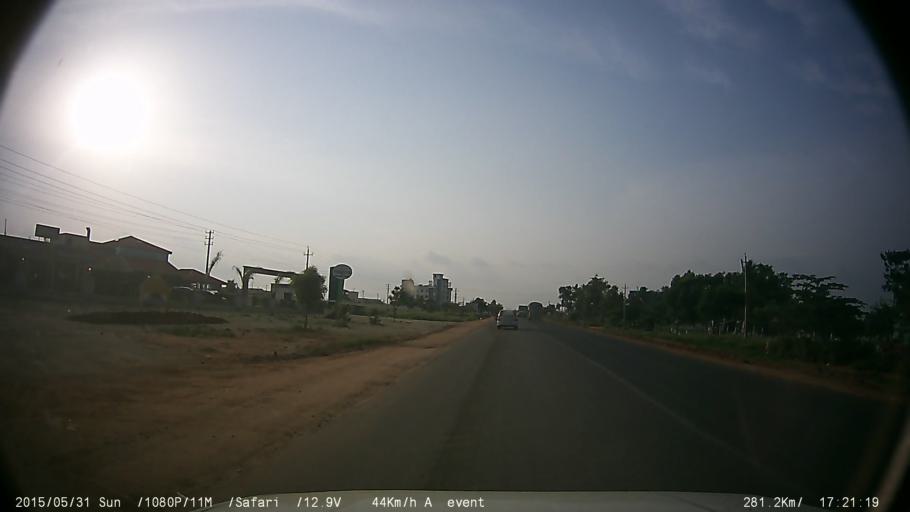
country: IN
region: Karnataka
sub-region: Chamrajnagar
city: Gundlupet
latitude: 11.8268
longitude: 76.6798
